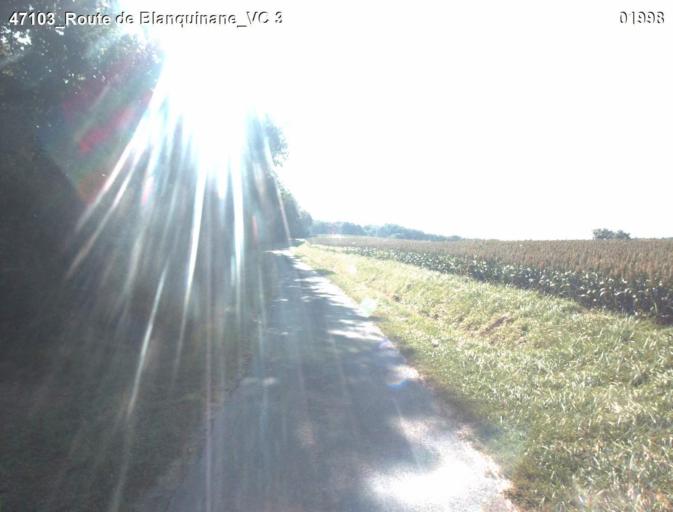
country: FR
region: Aquitaine
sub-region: Departement du Lot-et-Garonne
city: Nerac
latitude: 44.0855
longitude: 0.3413
